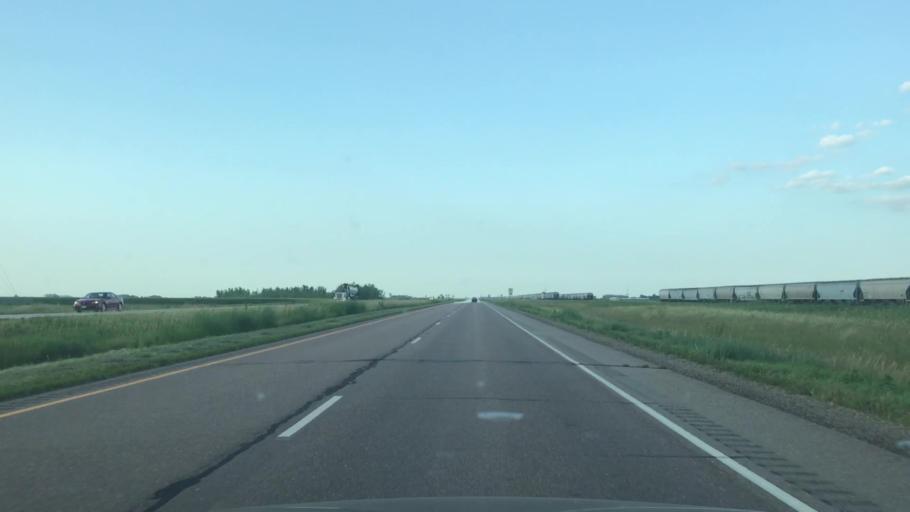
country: US
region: Minnesota
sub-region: Nobles County
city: Worthington
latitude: 43.7190
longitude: -95.4401
